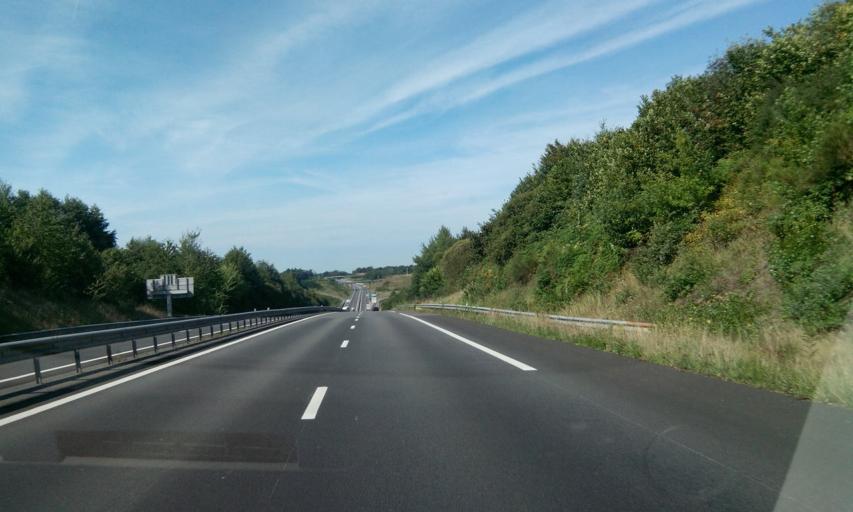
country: FR
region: Poitou-Charentes
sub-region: Departement de la Charente
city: Etagnac
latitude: 45.8953
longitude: 0.8263
